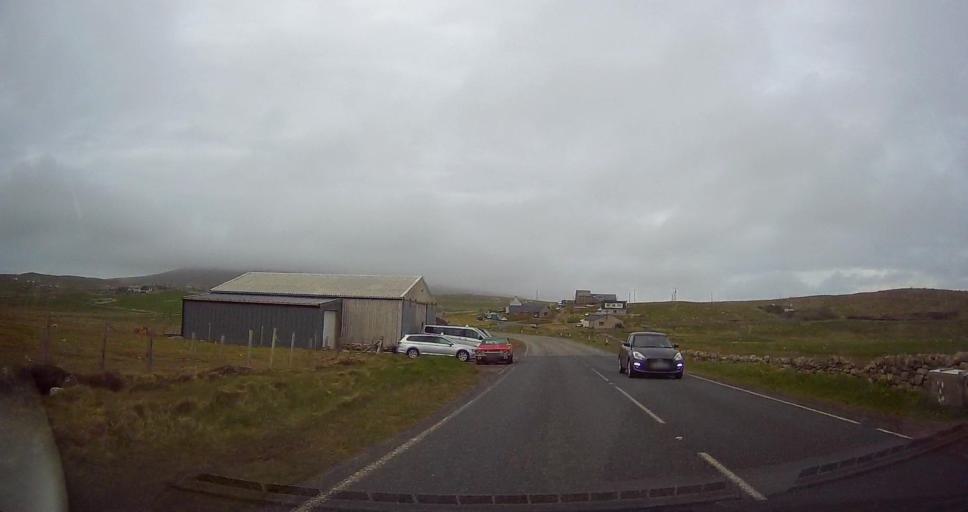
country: GB
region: Scotland
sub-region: Shetland Islands
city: Sandwick
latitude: 59.9253
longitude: -1.2979
